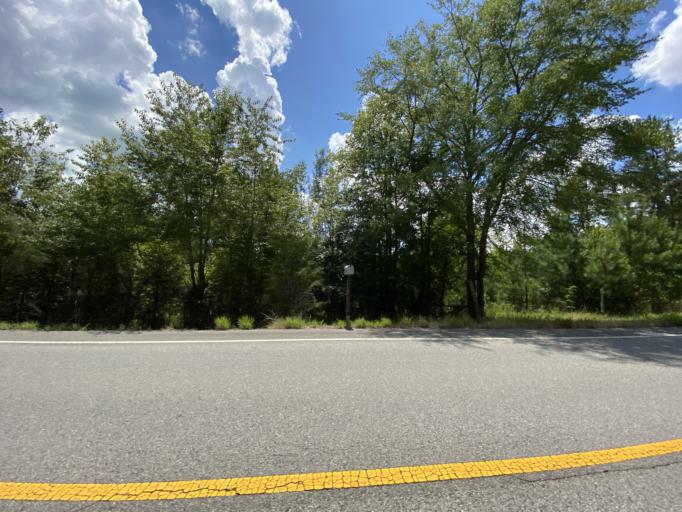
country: US
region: Alabama
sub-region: Lauderdale County
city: Underwood-Petersville
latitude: 34.9602
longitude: -87.8801
